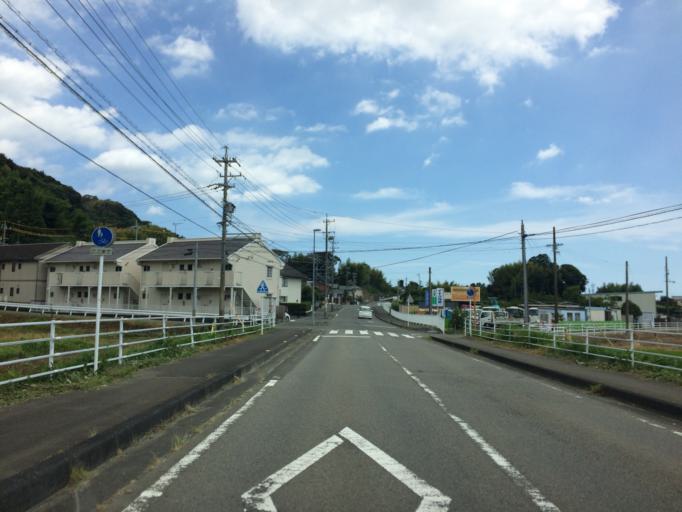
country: JP
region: Shizuoka
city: Yaizu
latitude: 34.8995
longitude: 138.2984
